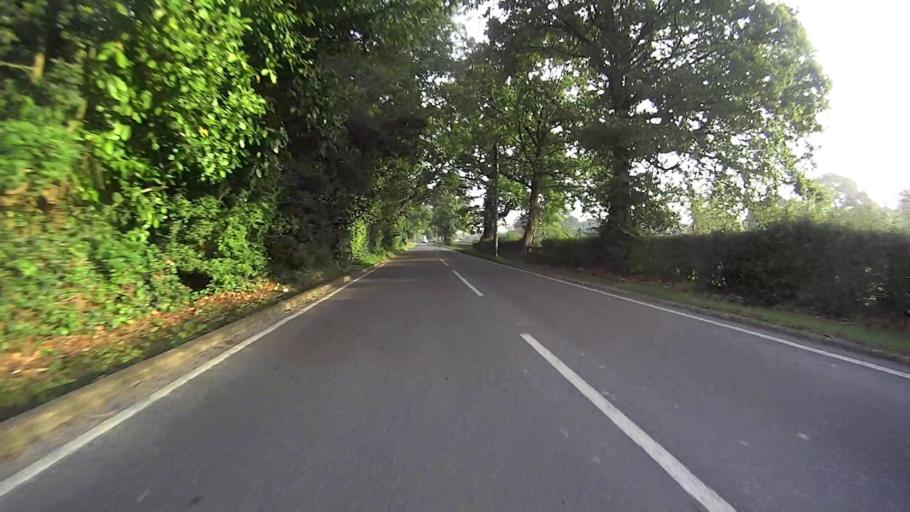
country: GB
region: England
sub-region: West Sussex
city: Copthorne
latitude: 51.1470
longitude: -0.1103
